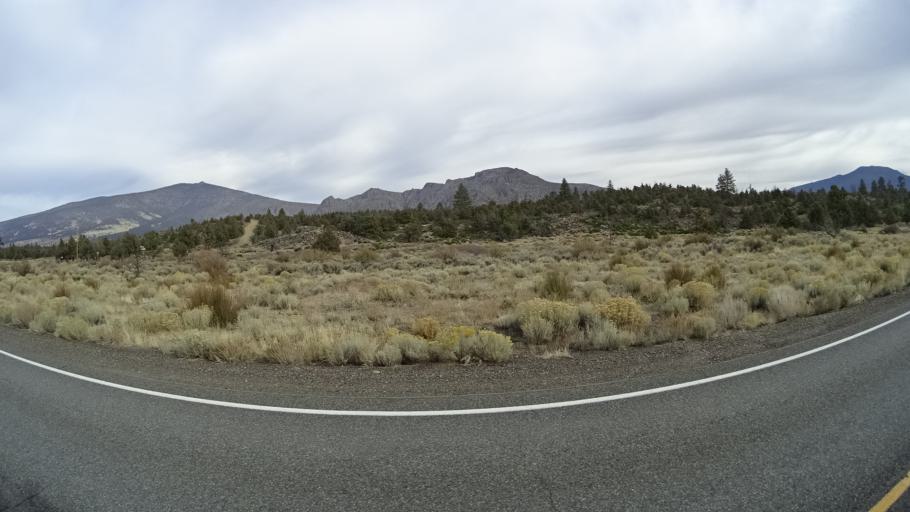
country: US
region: California
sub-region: Siskiyou County
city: Weed
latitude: 41.5641
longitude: -122.2632
